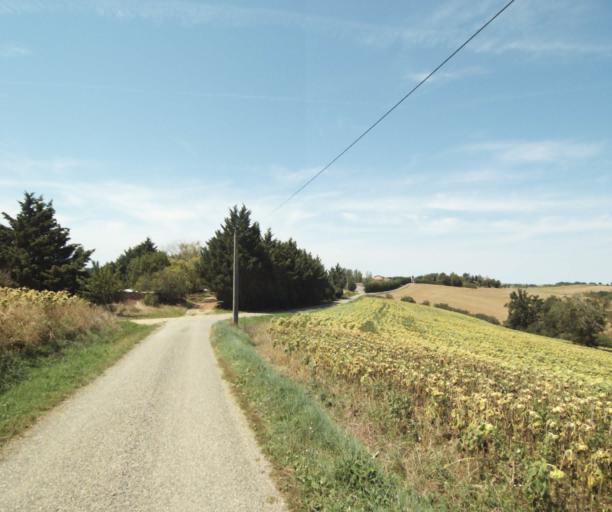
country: FR
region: Midi-Pyrenees
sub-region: Departement de l'Ariege
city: Lezat-sur-Leze
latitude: 43.2652
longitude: 1.3143
